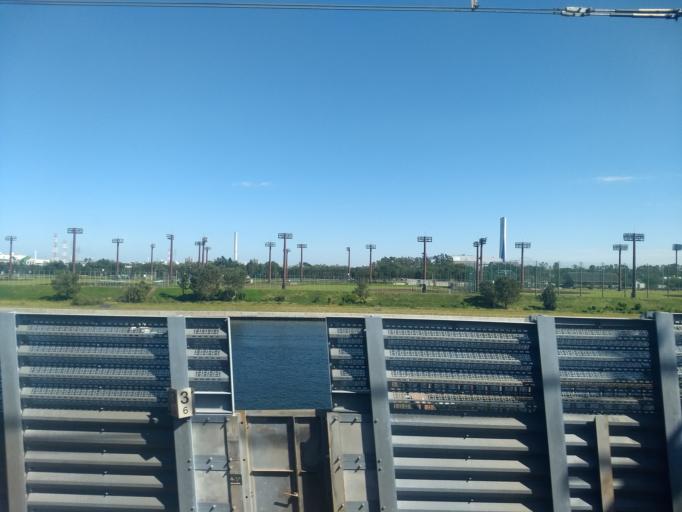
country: JP
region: Tokyo
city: Urayasu
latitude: 35.6513
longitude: 139.8197
